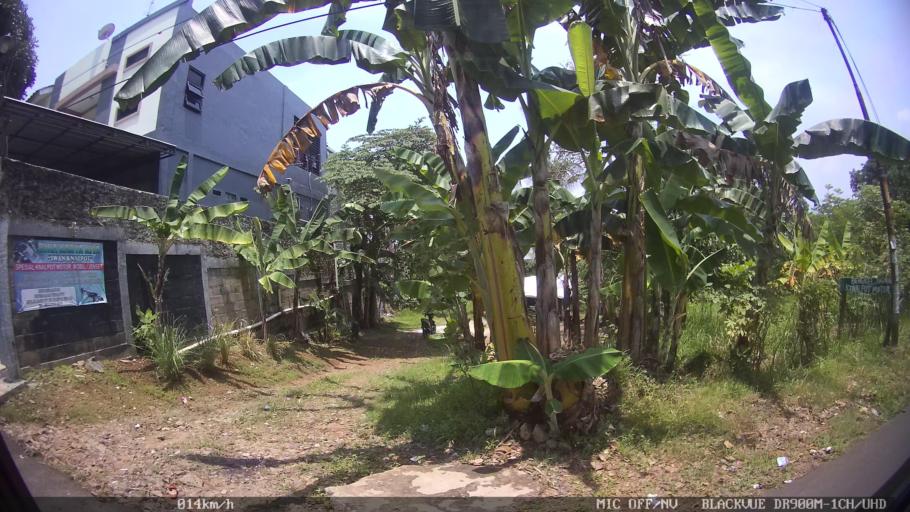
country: ID
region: Lampung
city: Bandarlampung
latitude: -5.4356
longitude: 105.2501
